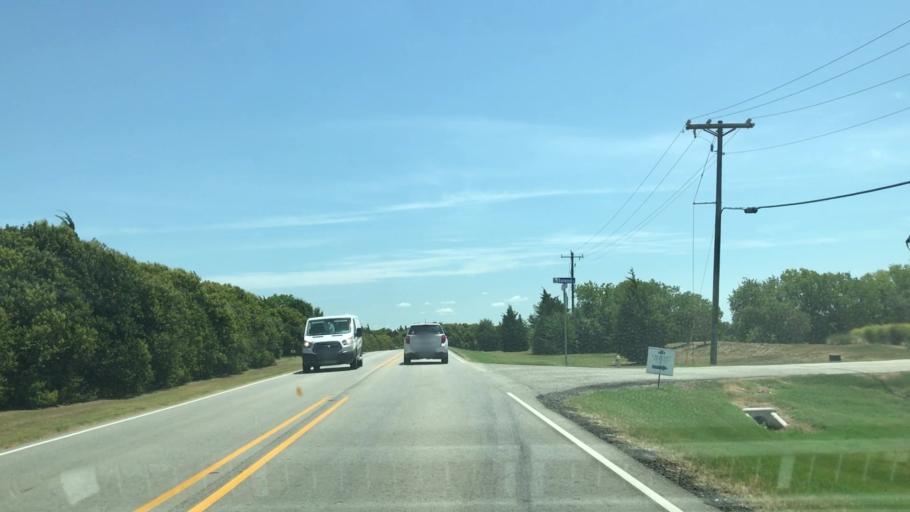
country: US
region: Texas
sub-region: Collin County
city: Lucas
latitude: 33.0750
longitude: -96.5746
